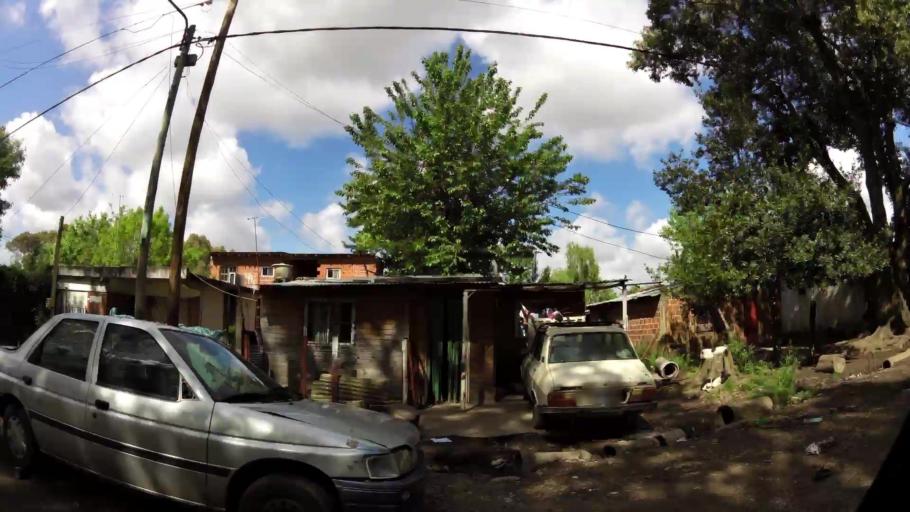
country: AR
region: Buenos Aires
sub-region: Partido de Quilmes
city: Quilmes
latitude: -34.8258
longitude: -58.1673
